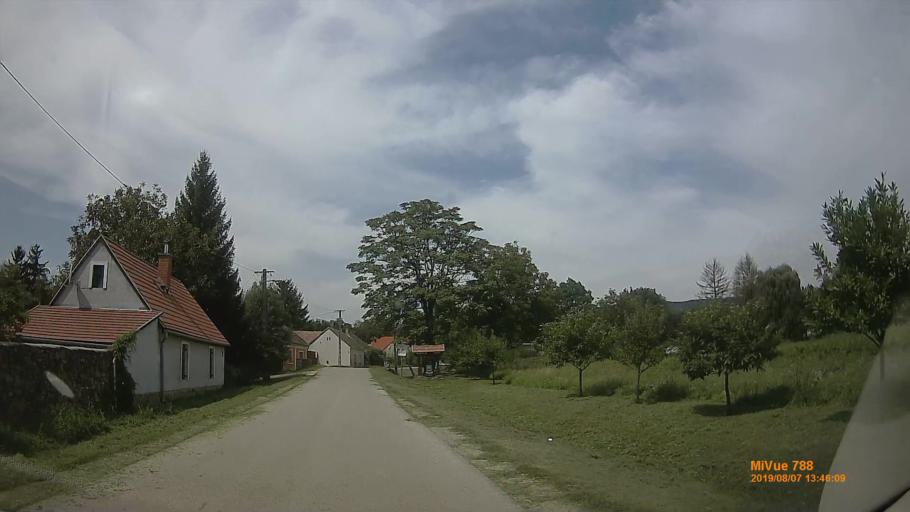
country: HU
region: Zala
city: Cserszegtomaj
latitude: 46.8847
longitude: 17.1951
